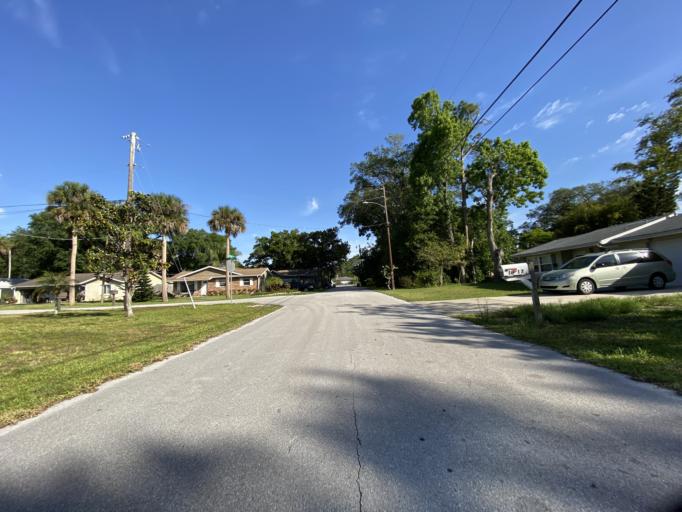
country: US
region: Florida
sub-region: Volusia County
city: South Daytona
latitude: 29.1785
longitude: -81.0176
